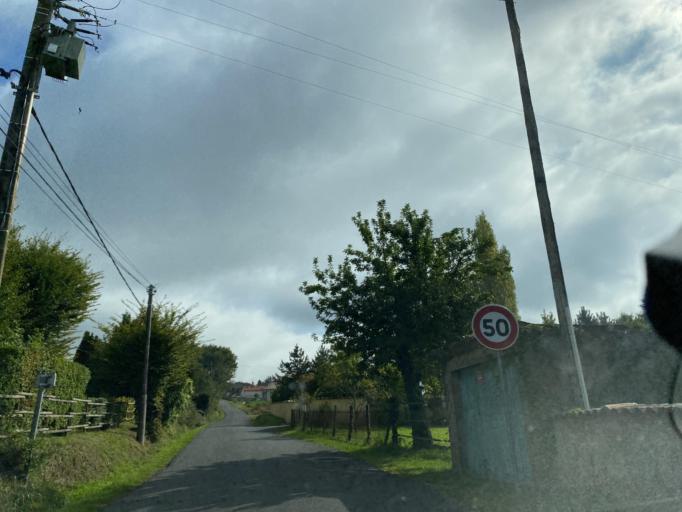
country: FR
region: Auvergne
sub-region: Departement du Puy-de-Dome
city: Escoutoux
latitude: 45.8312
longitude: 3.5457
